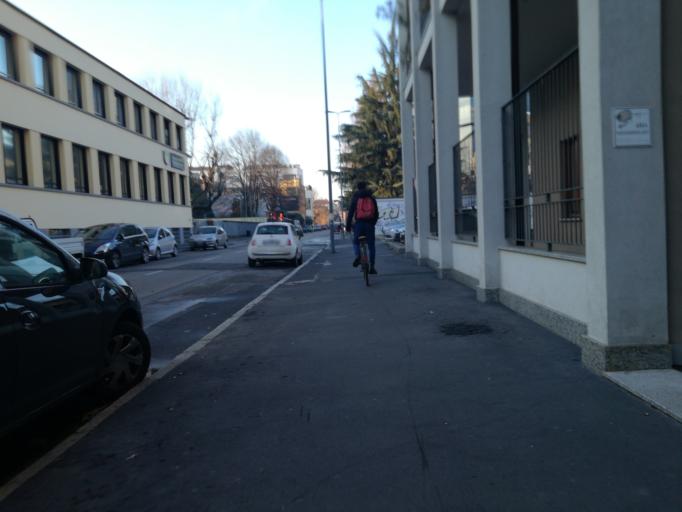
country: IT
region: Lombardy
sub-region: Citta metropolitana di Milano
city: Romano Banco
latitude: 45.4406
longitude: 9.1459
